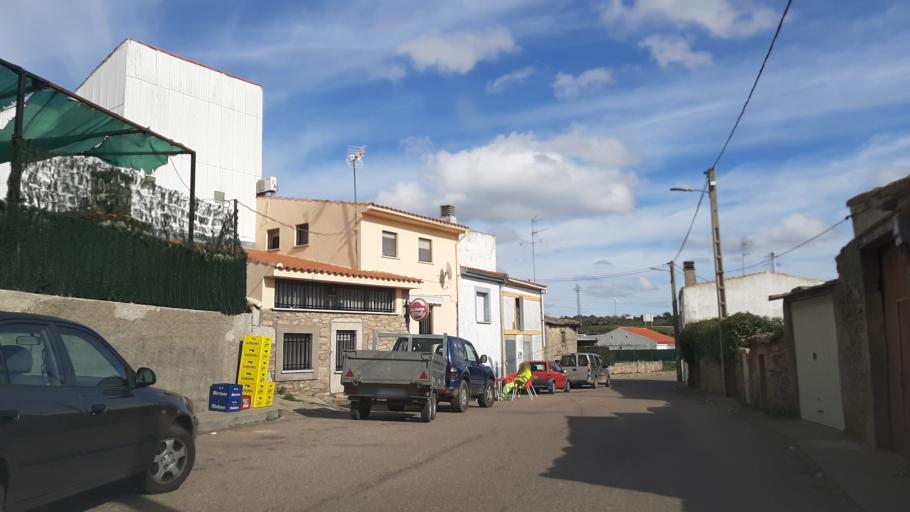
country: ES
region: Castille and Leon
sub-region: Provincia de Salamanca
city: Villarino de los Aires
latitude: 41.2366
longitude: -6.5211
